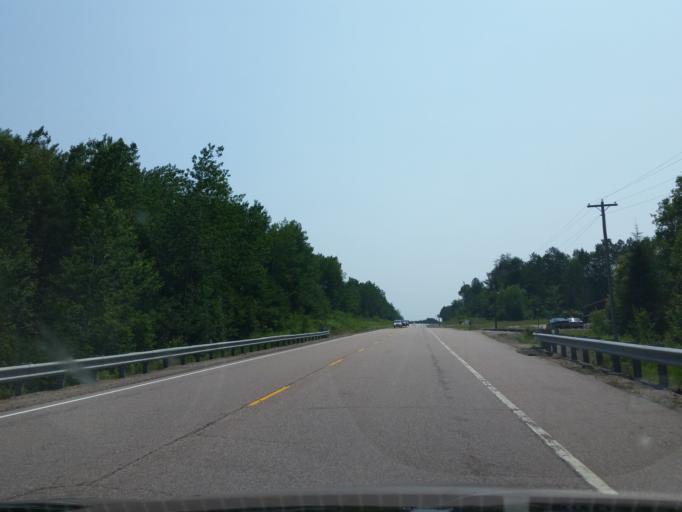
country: CA
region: Ontario
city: Deep River
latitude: 46.1864
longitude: -77.8645
